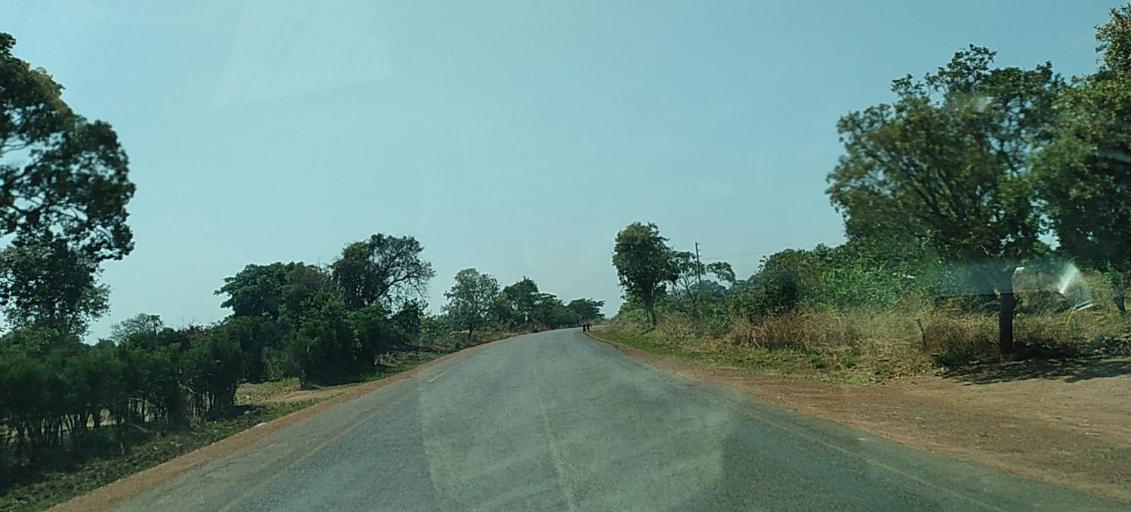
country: ZM
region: North-Western
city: Solwezi
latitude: -12.3221
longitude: 25.8772
